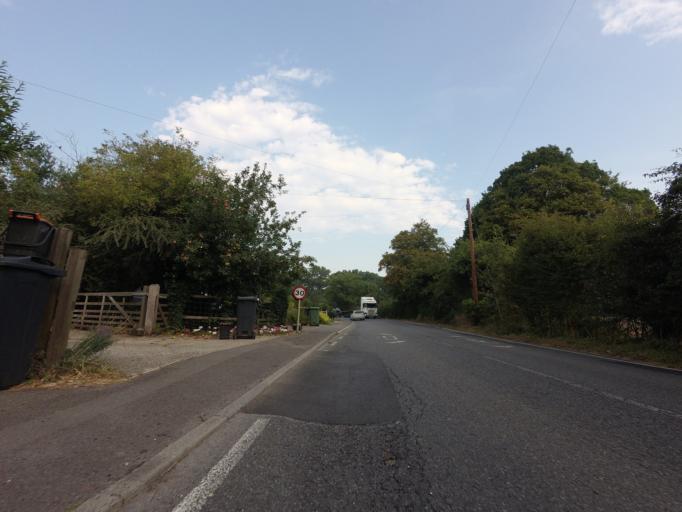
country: GB
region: England
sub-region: Kent
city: Tenterden
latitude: 51.1252
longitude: 0.7622
